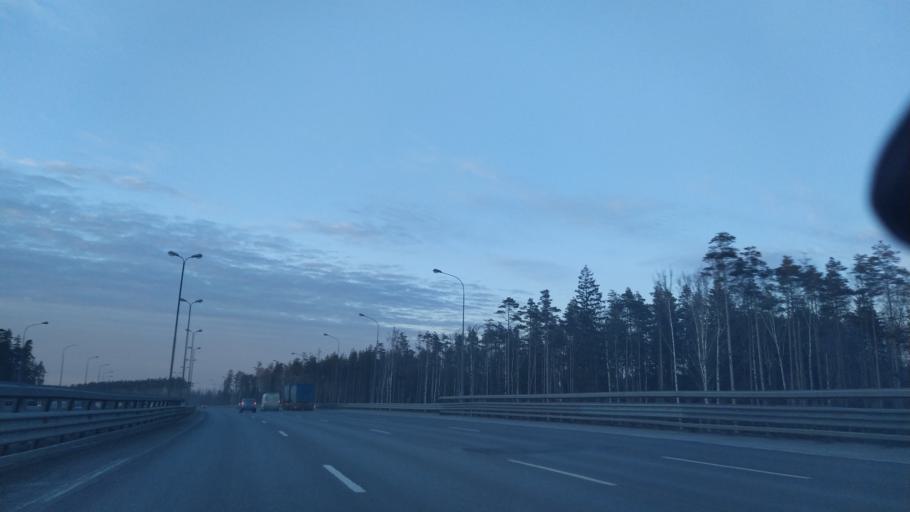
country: RU
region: Leningrad
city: Yanino Vtoroye
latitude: 59.9642
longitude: 30.5538
